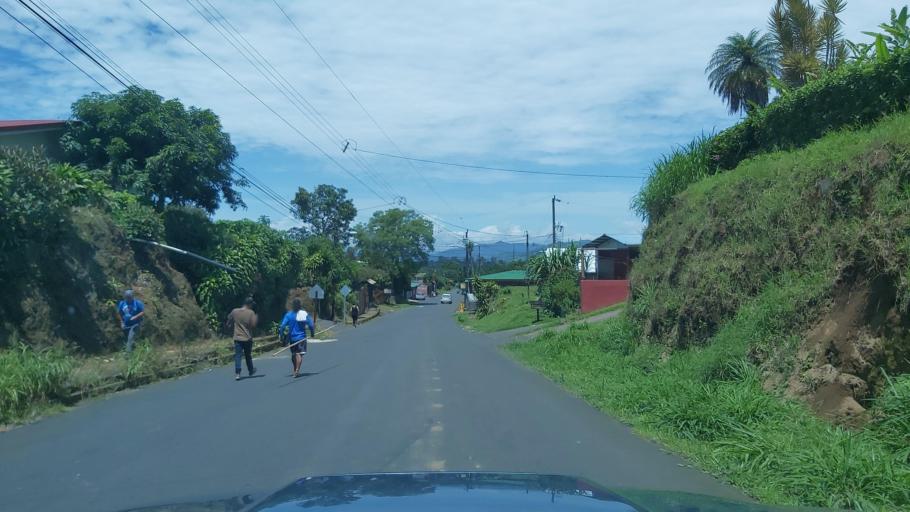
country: CR
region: Alajuela
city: San Juan
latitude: 10.0926
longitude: -84.3403
